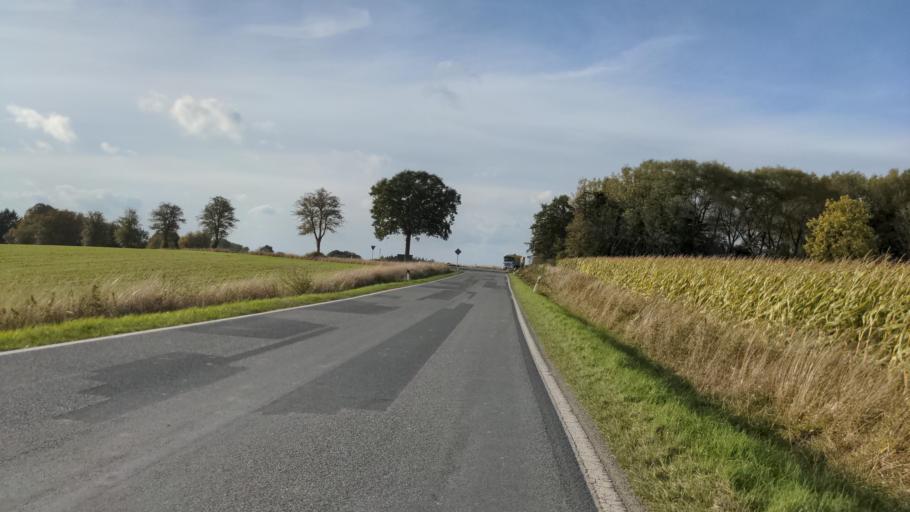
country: DE
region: Schleswig-Holstein
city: Monkhagen
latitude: 53.9557
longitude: 10.5303
